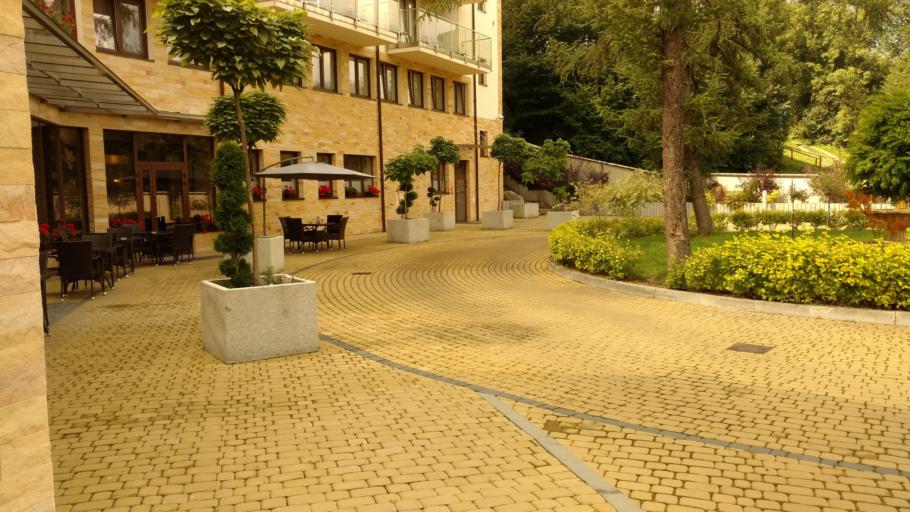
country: PL
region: Lesser Poland Voivodeship
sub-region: Powiat myslenicki
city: Skomielna Czarna
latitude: 49.7323
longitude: 19.8228
